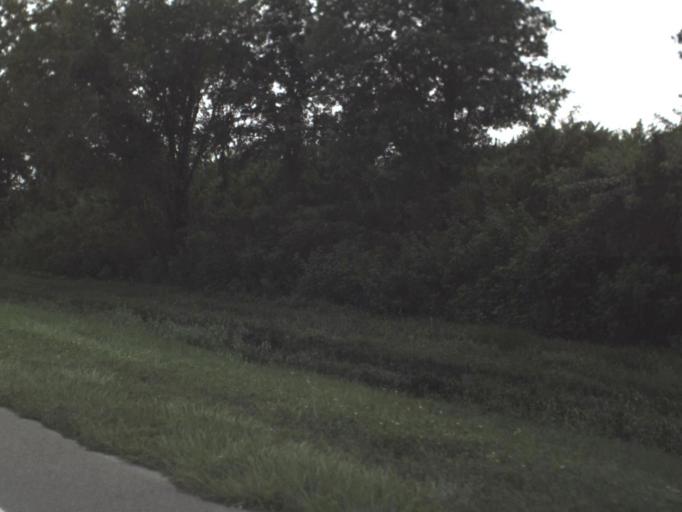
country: US
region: Florida
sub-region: Hillsborough County
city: Wimauma
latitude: 27.5941
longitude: -82.2665
